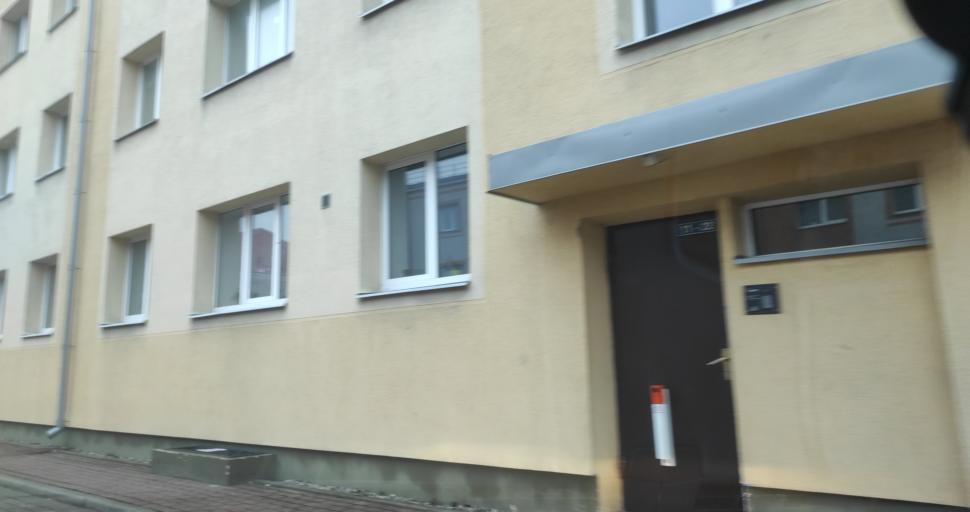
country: LV
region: Ventspils
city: Ventspils
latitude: 57.3883
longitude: 21.5499
